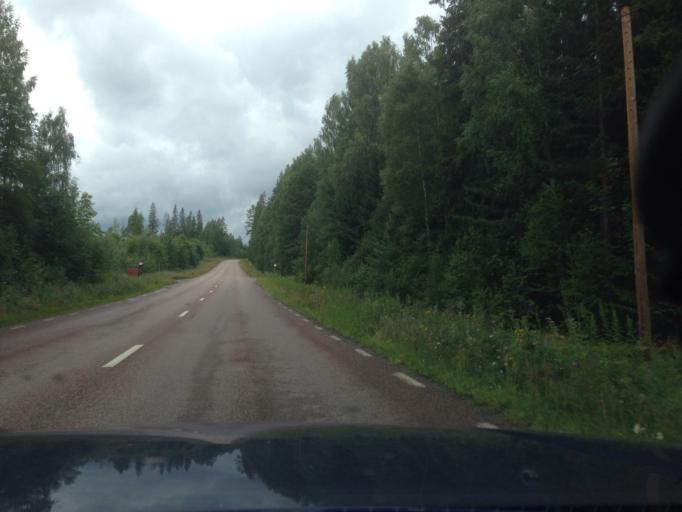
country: SE
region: Dalarna
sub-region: Ludvika Kommun
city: Ludvika
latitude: 60.1363
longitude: 15.1484
